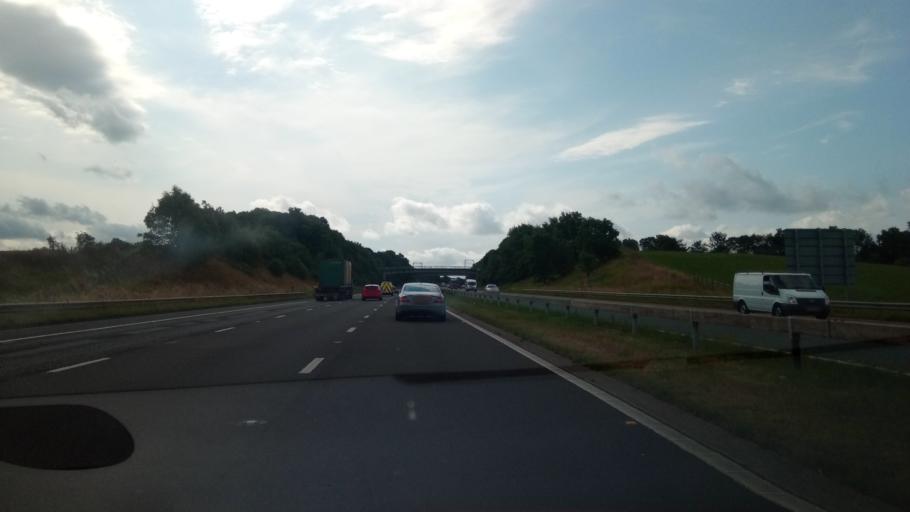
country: GB
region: England
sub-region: Cumbria
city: Penrith
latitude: 54.6389
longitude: -2.7318
